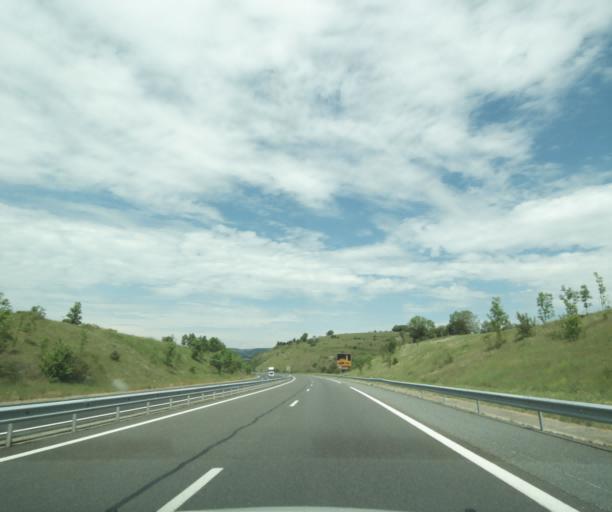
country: FR
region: Midi-Pyrenees
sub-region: Departement de l'Aveyron
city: Severac-le-Chateau
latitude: 44.3101
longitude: 3.1032
